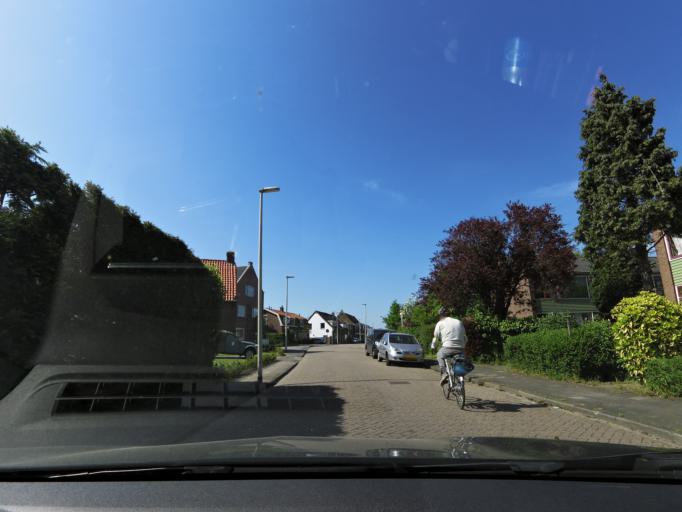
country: NL
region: South Holland
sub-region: Gemeente Albrandswaard
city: Rhoon
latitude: 51.8519
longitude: 4.4212
